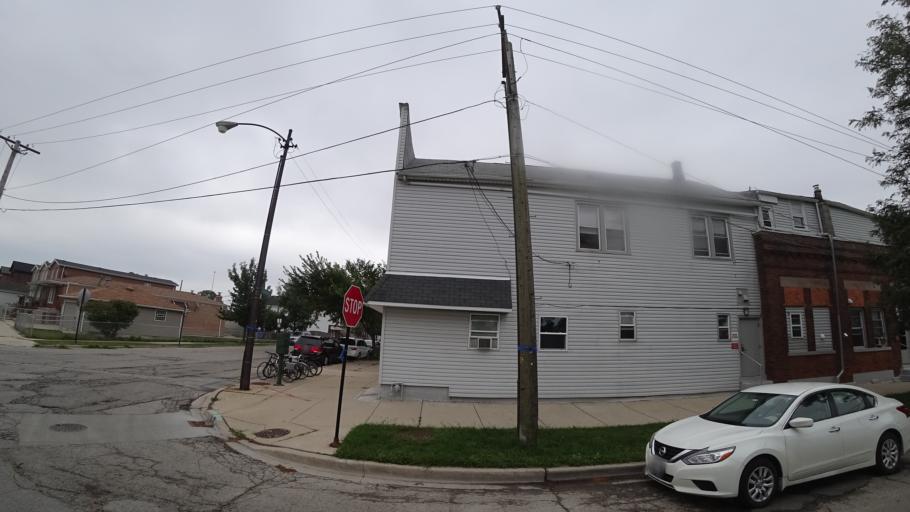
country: US
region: Illinois
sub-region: Cook County
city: Chicago
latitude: 41.8464
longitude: -87.6569
